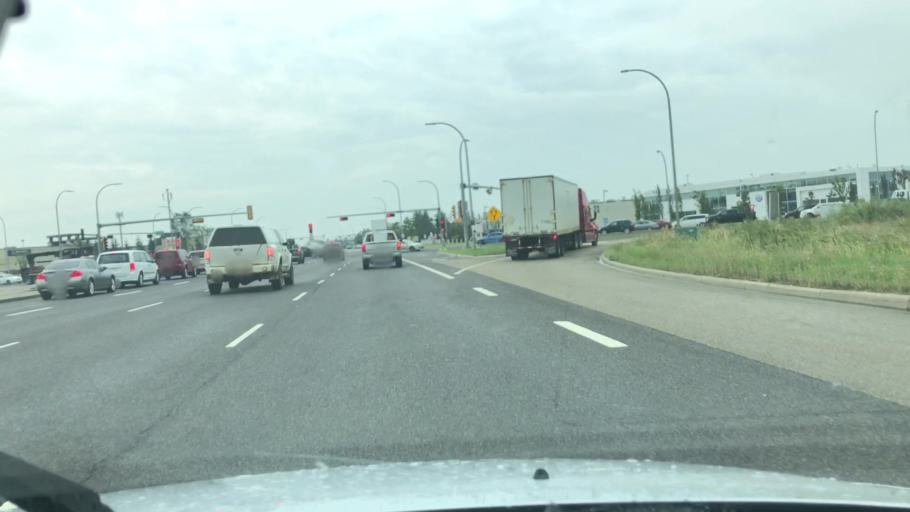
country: CA
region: Alberta
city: St. Albert
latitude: 53.6003
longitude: -113.5760
